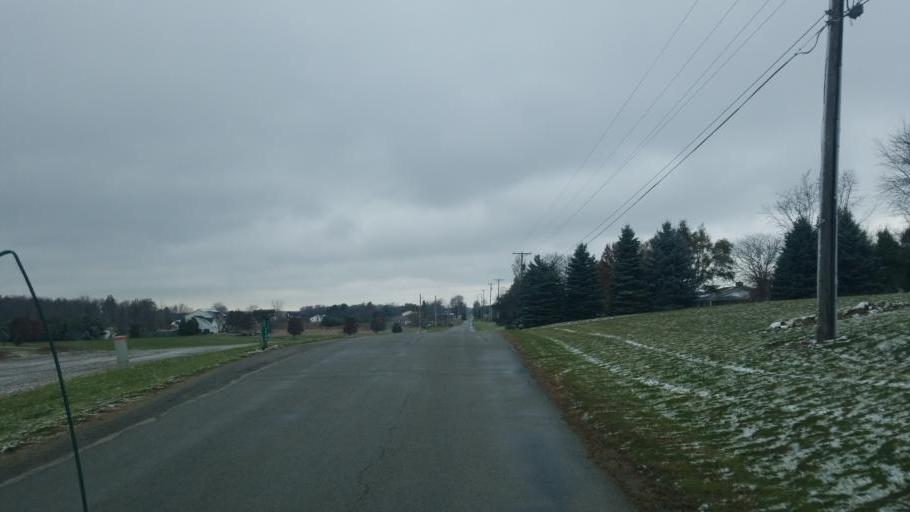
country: US
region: Ohio
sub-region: Richland County
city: Shelby
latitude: 40.8657
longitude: -82.5956
